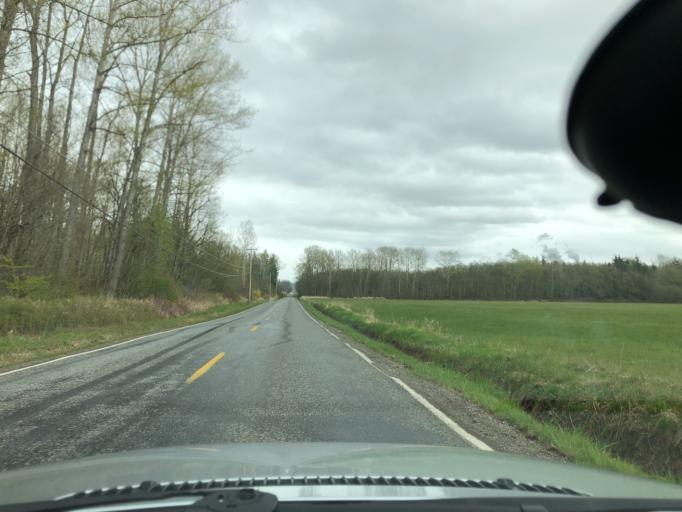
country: US
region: Washington
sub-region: Whatcom County
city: Birch Bay
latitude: 48.8924
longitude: -122.7598
